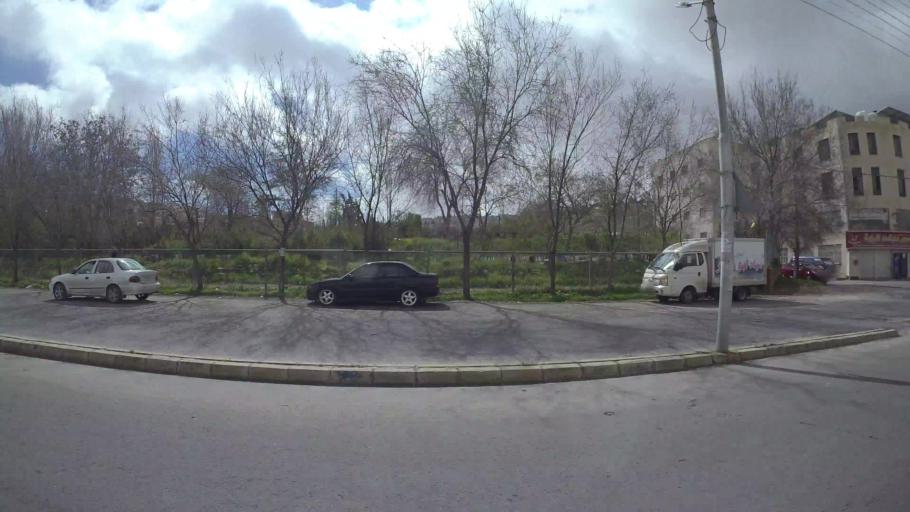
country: JO
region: Amman
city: Al Jubayhah
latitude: 32.0624
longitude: 35.8827
